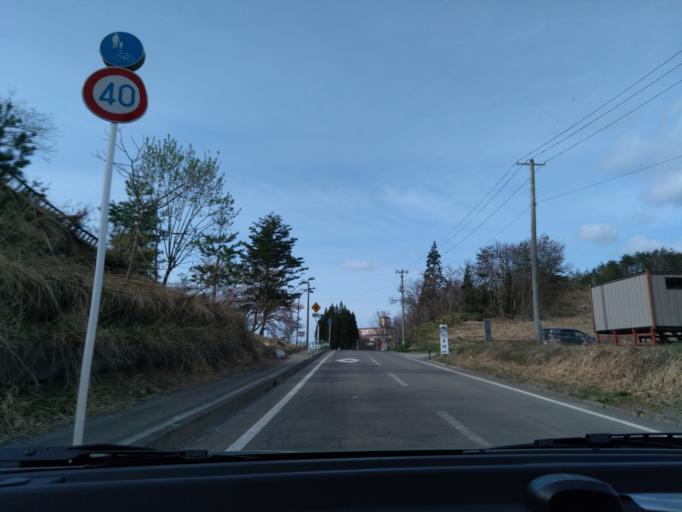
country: JP
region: Akita
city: Yokotemachi
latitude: 39.3243
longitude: 140.5734
